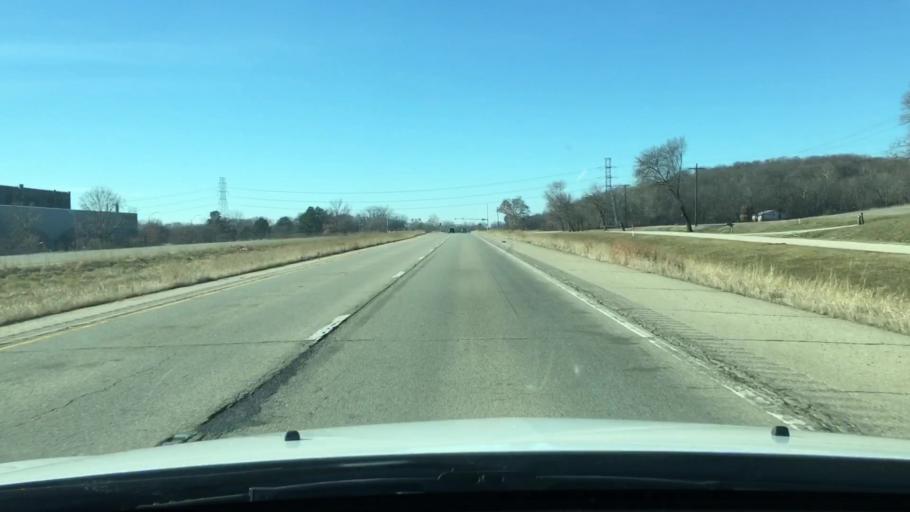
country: US
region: Illinois
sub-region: Peoria County
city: Glasford
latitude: 40.5624
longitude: -89.7465
